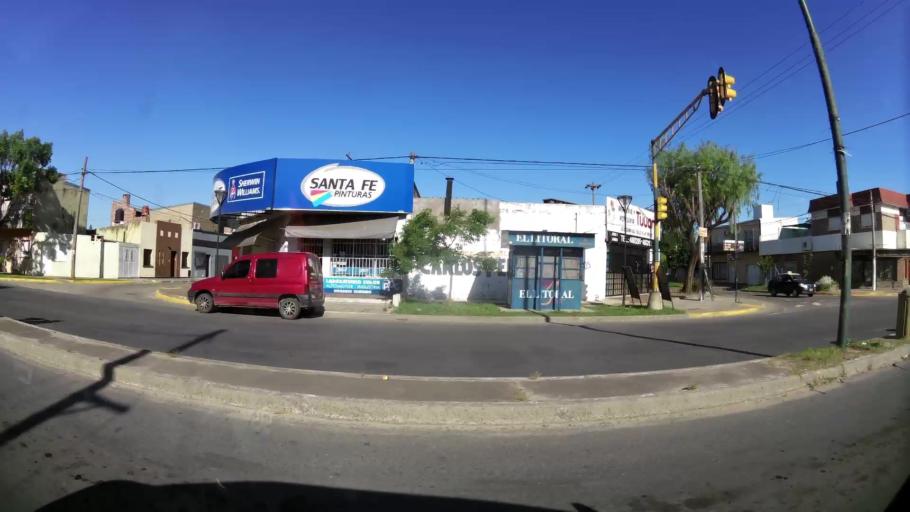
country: AR
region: Santa Fe
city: Santa Fe de la Vera Cruz
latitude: -31.6089
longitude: -60.7042
